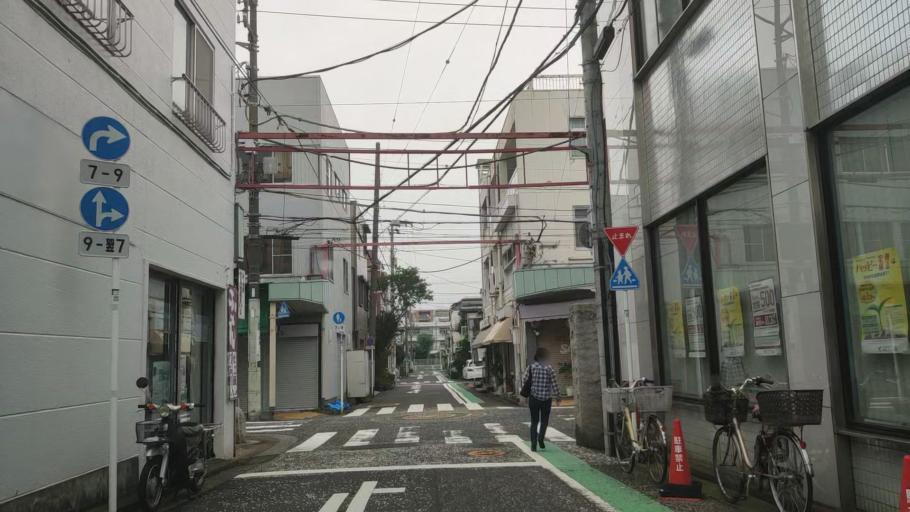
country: JP
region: Kanagawa
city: Yokohama
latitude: 35.4522
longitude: 139.6161
